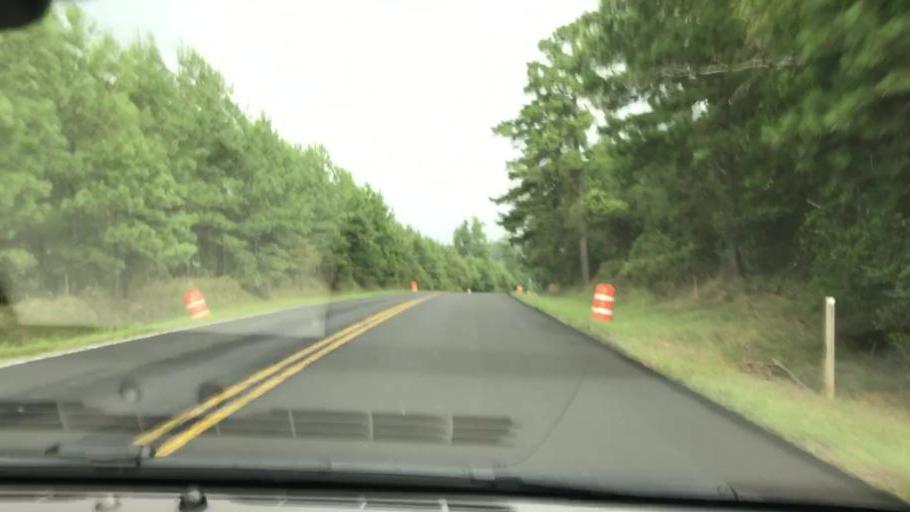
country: US
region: Georgia
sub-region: Clay County
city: Fort Gaines
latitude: 31.5131
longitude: -85.0220
